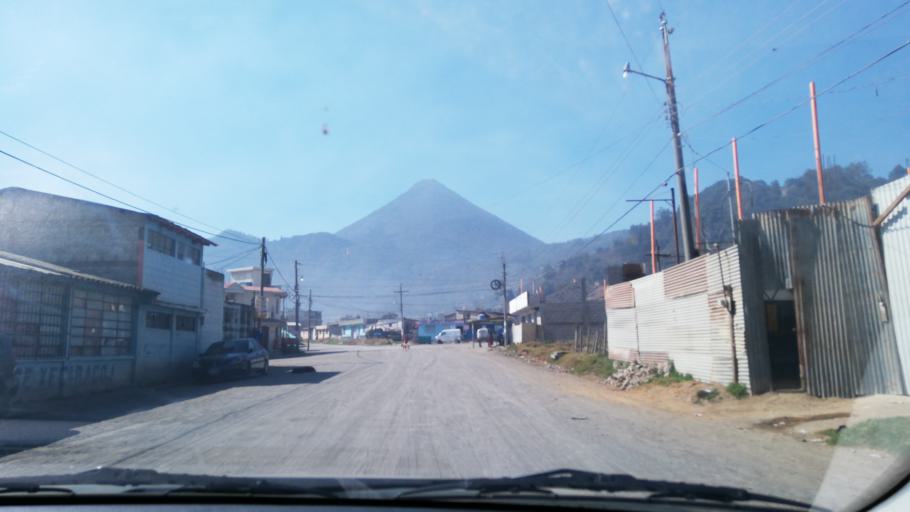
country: GT
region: Quetzaltenango
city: Quetzaltenango
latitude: 14.8039
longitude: -91.5515
